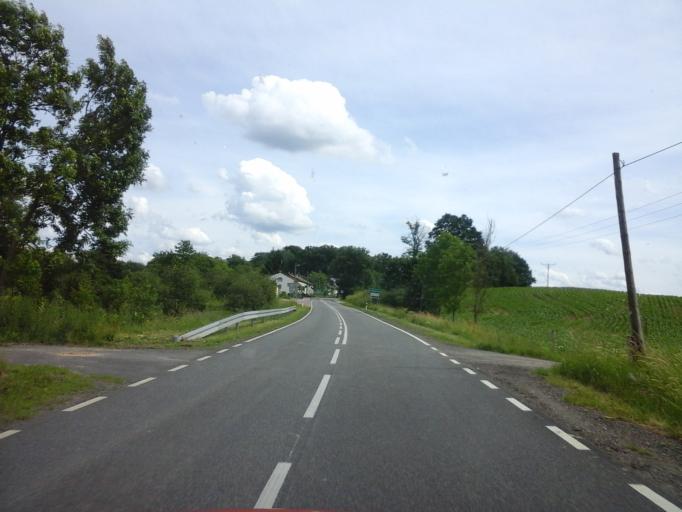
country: PL
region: West Pomeranian Voivodeship
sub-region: Powiat lobeski
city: Wegorzyno
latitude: 53.5156
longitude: 15.5726
